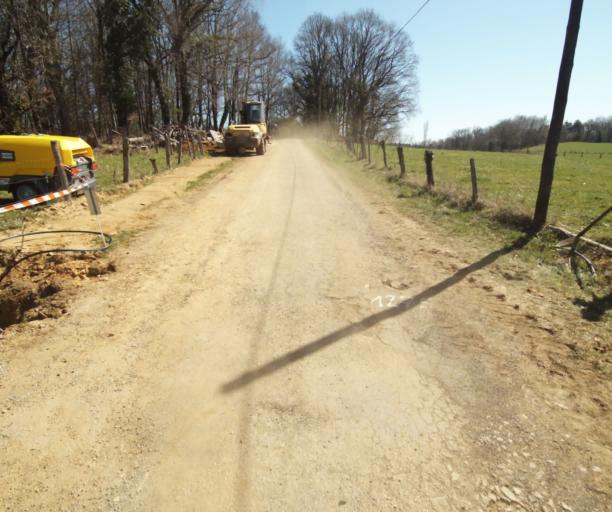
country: FR
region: Limousin
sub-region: Departement de la Correze
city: Saint-Clement
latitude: 45.3715
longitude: 1.6832
